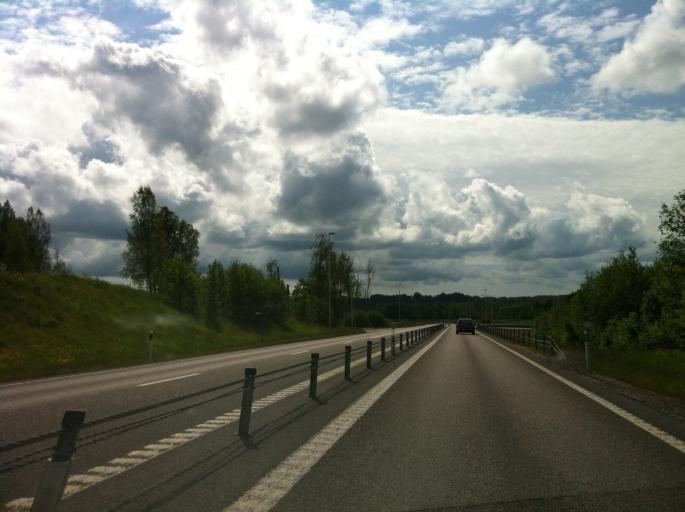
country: SE
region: Vaermland
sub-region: Karlstads Kommun
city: Edsvalla
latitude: 59.5419
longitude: 13.2012
